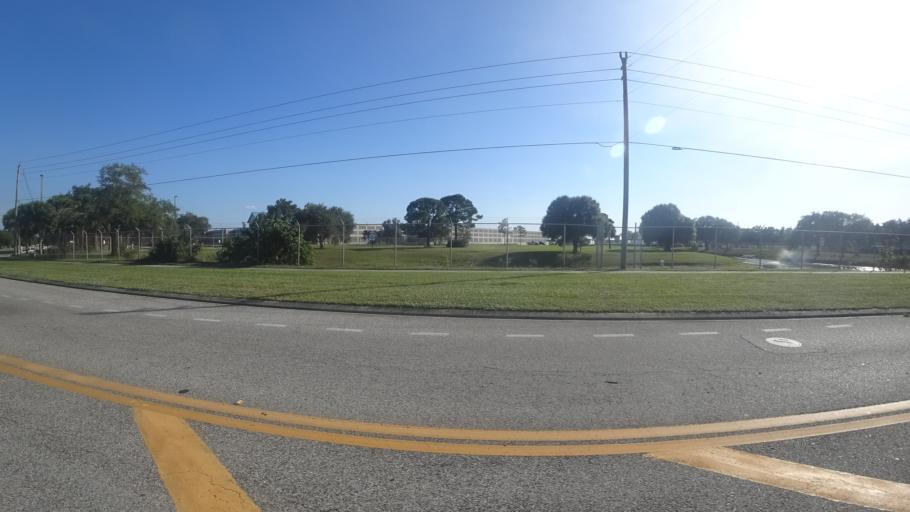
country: US
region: Florida
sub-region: Manatee County
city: Whitfield
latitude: 27.4076
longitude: -82.5585
